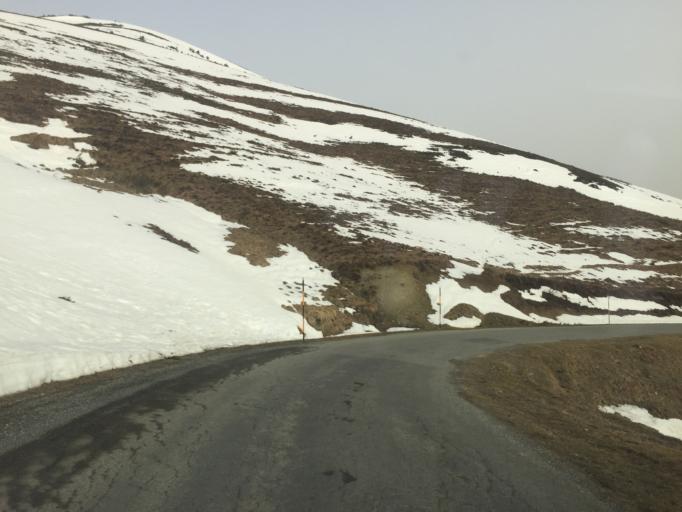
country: FR
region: Midi-Pyrenees
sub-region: Departement des Hautes-Pyrenees
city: Saint-Lary-Soulan
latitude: 42.7963
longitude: 0.3844
